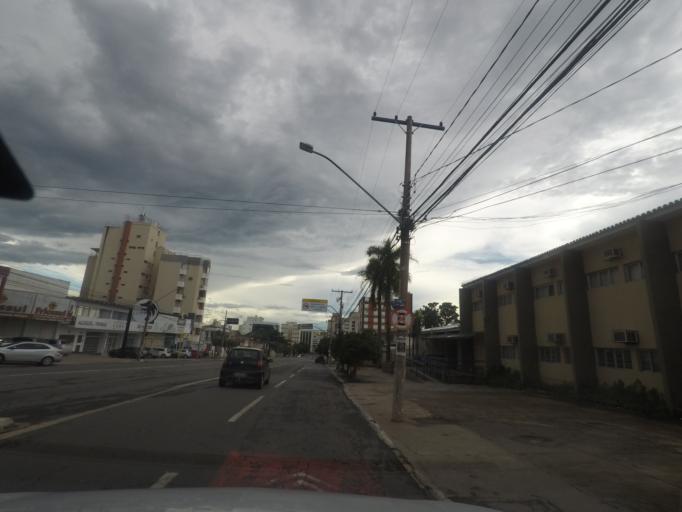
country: BR
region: Goias
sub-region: Goiania
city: Goiania
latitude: -16.6878
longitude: -49.2540
